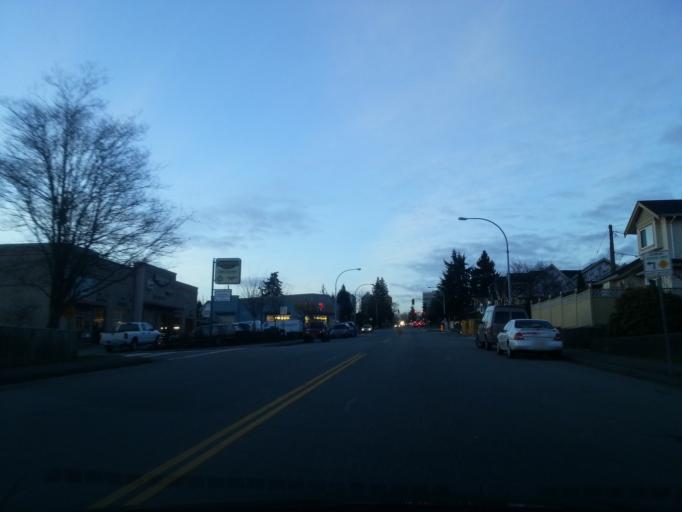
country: CA
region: British Columbia
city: New Westminster
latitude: 49.2039
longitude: -122.9497
